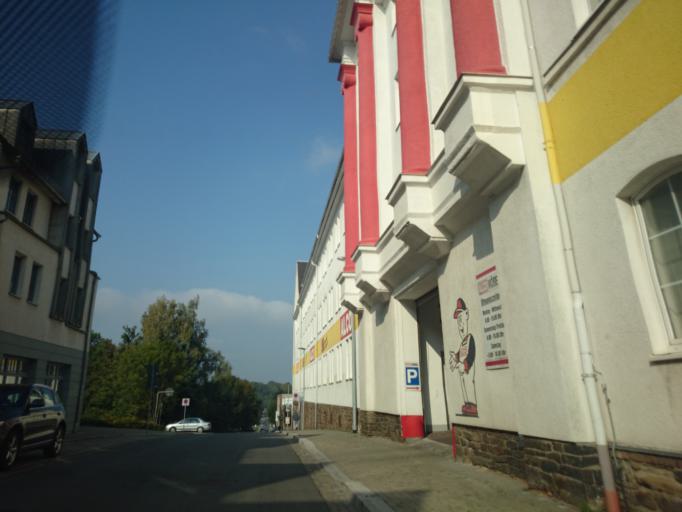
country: DE
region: Saxony
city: Brand-Erbisdorf
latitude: 50.8716
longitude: 13.3243
